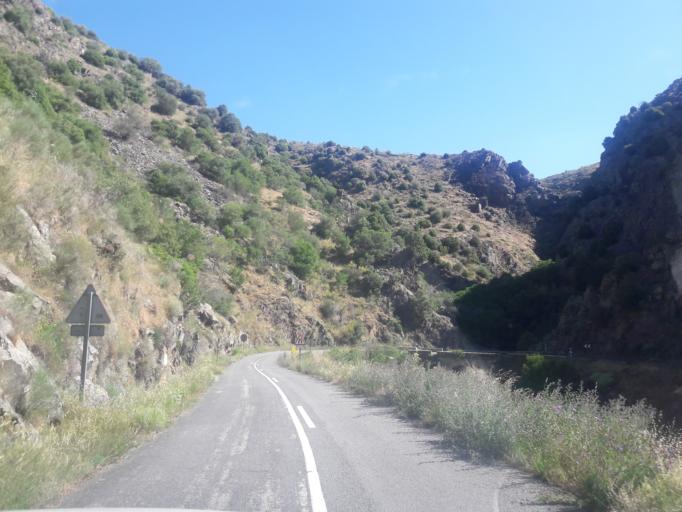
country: ES
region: Castille and Leon
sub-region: Provincia de Salamanca
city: Saucelle
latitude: 41.0383
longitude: -6.7368
